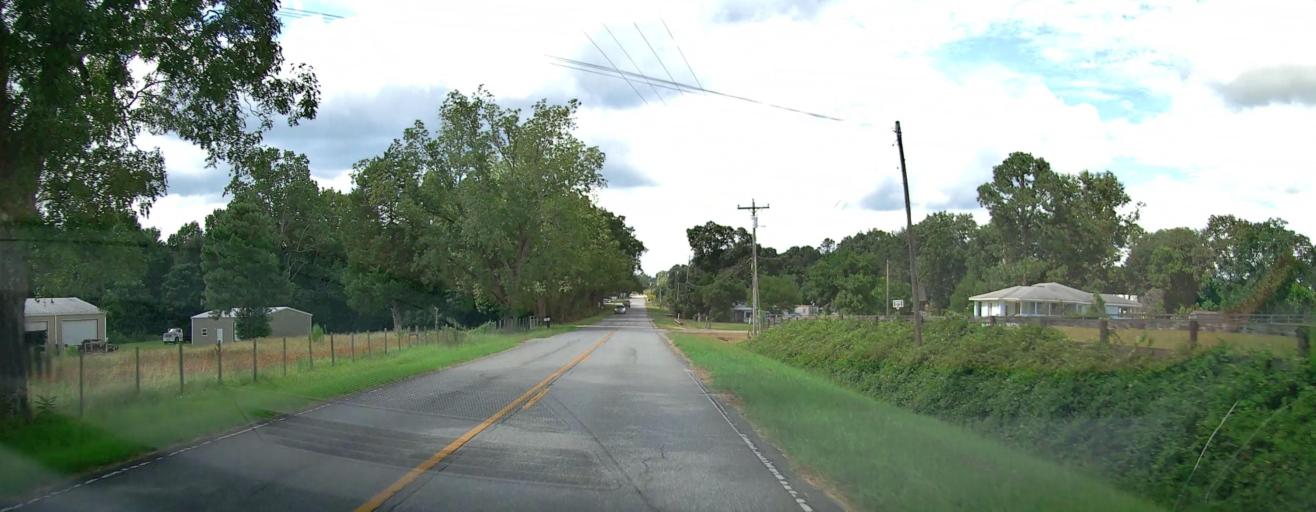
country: US
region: Georgia
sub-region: Chattahoochee County
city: Cusseta
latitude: 32.2961
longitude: -84.7691
